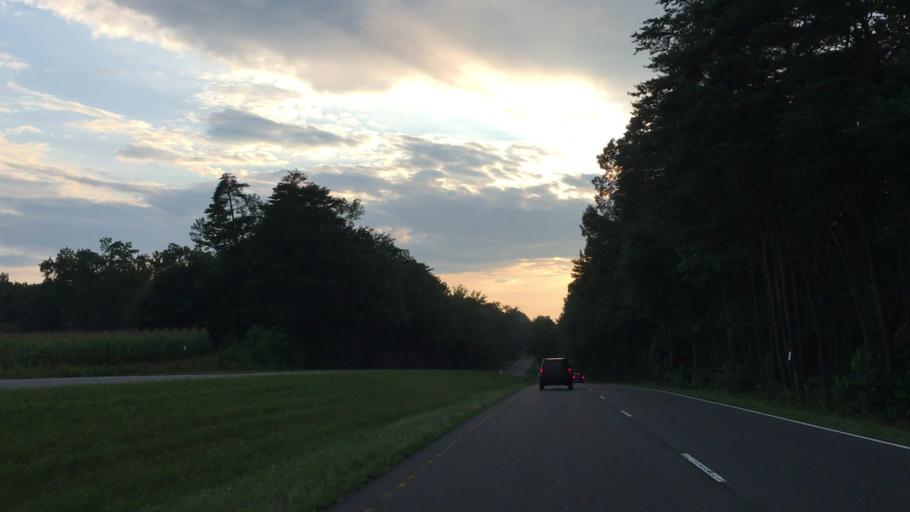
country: US
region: Virginia
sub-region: Spotsylvania County
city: Spotsylvania
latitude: 38.3094
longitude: -77.6405
